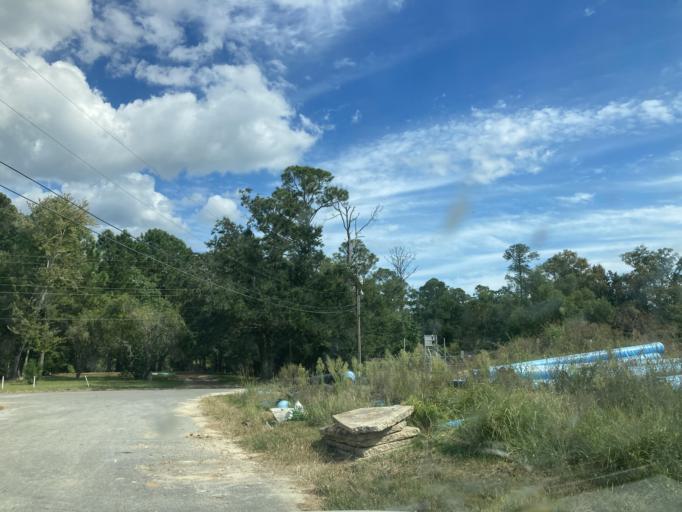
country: US
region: Mississippi
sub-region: Jackson County
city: Saint Martin
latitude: 30.4372
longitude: -88.8764
